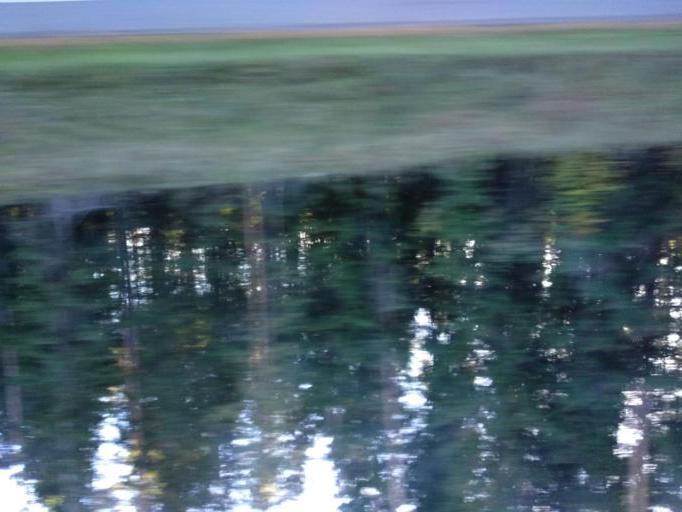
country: EE
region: Polvamaa
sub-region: Polva linn
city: Polva
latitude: 58.0358
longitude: 27.0659
